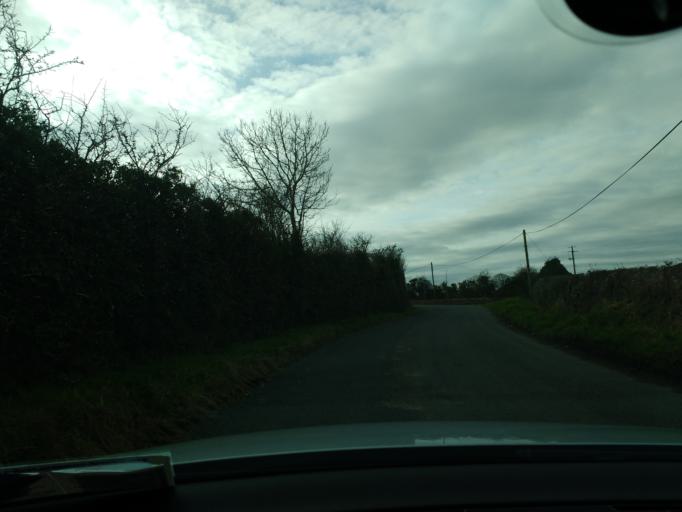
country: IE
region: Leinster
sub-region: Laois
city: Rathdowney
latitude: 52.6789
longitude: -7.6063
